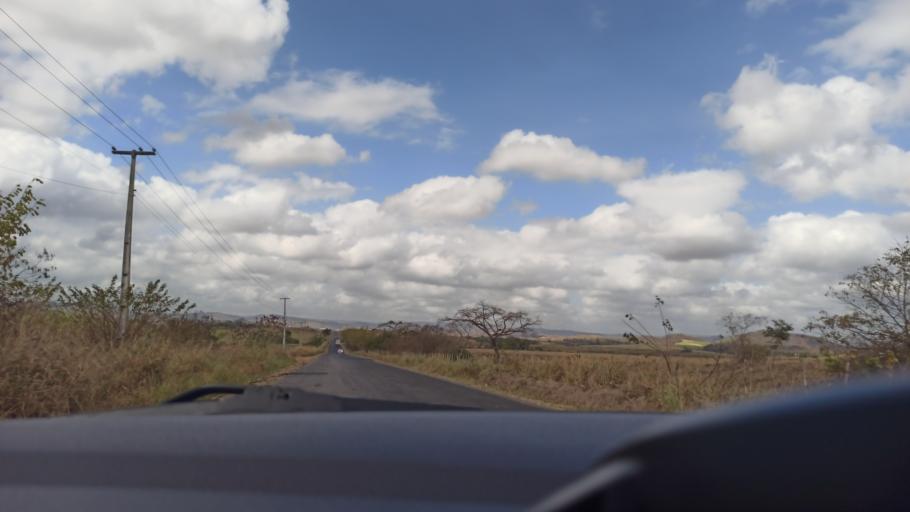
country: BR
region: Pernambuco
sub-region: Timbauba
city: Timbauba
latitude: -7.4739
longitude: -35.2783
